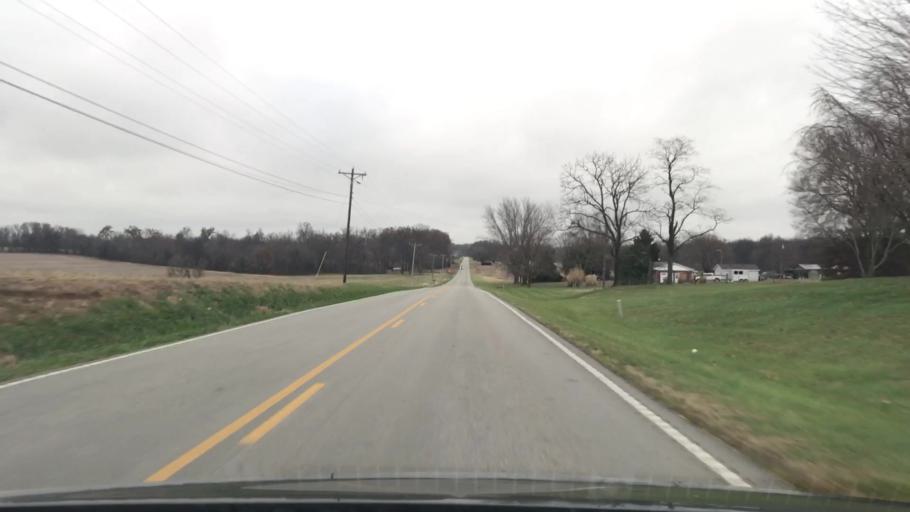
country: US
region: Kentucky
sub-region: Todd County
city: Guthrie
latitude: 36.7100
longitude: -87.1939
